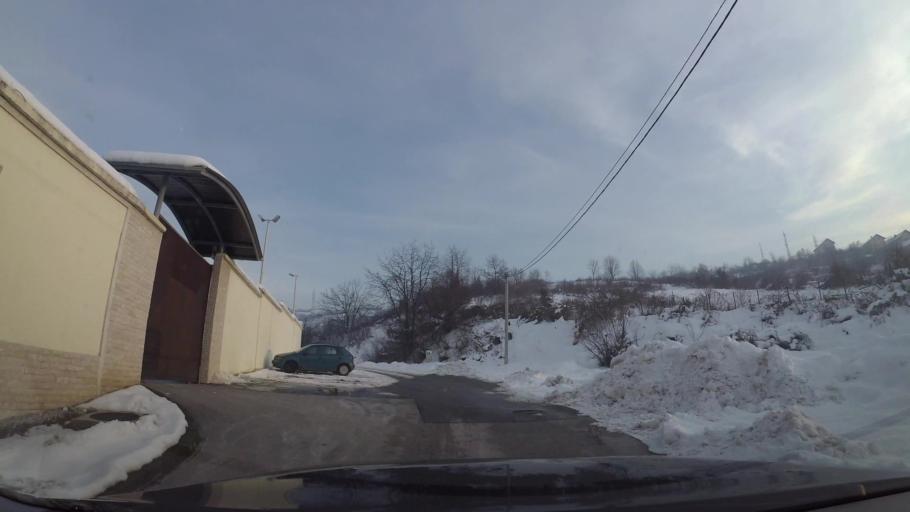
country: BA
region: Federation of Bosnia and Herzegovina
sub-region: Kanton Sarajevo
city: Sarajevo
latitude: 43.8388
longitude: 18.3525
